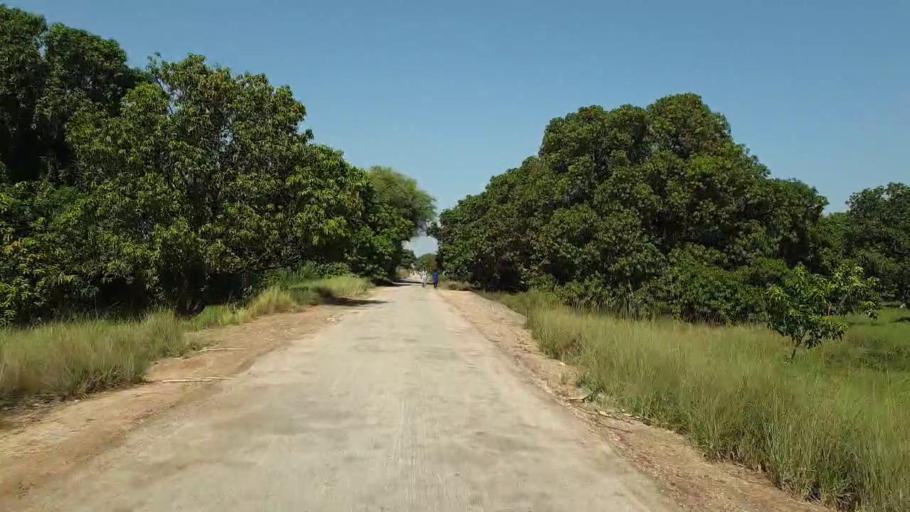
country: PK
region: Sindh
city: Tando Jam
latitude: 25.4358
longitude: 68.4602
